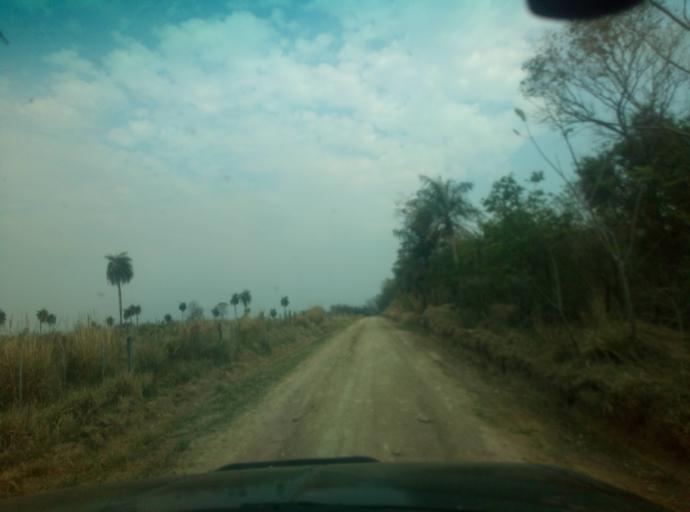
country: PY
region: Caaguazu
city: San Joaquin
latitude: -25.0859
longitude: -56.1431
